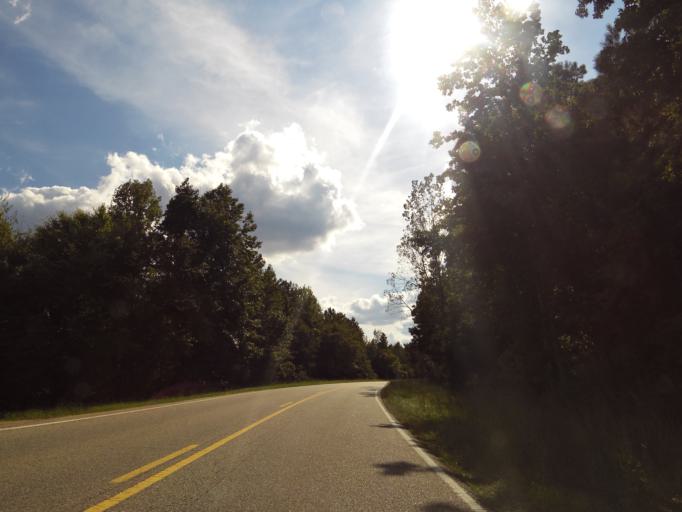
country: US
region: Alabama
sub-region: Dallas County
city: Selmont-West Selmont
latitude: 32.1691
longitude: -87.0542
